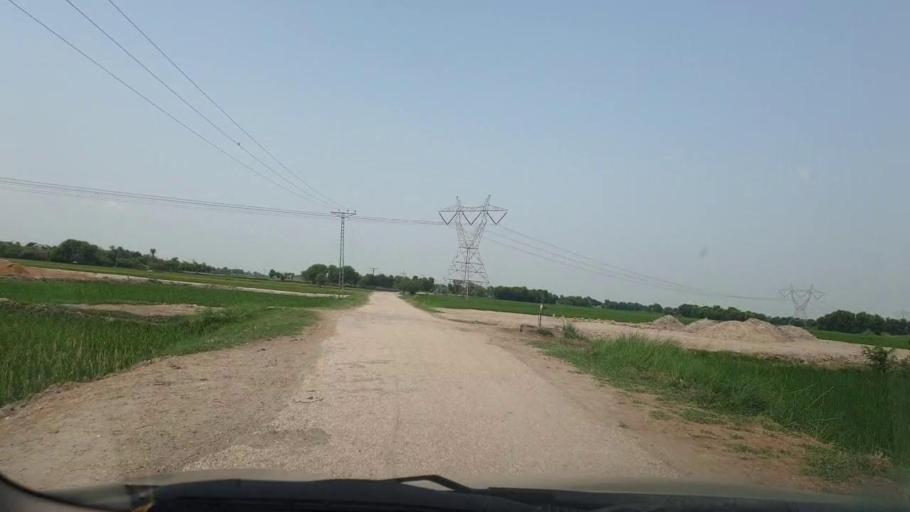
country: PK
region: Sindh
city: Larkana
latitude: 27.5793
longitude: 68.1431
